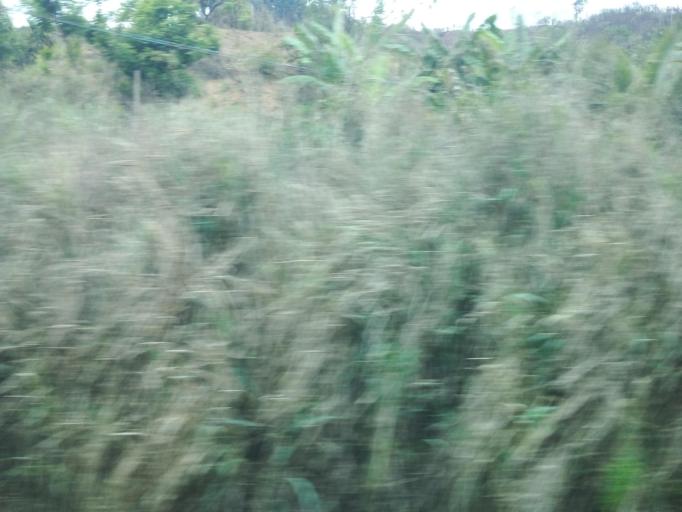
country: BR
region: Minas Gerais
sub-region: Timoteo
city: Timoteo
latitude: -19.5391
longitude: -42.6760
